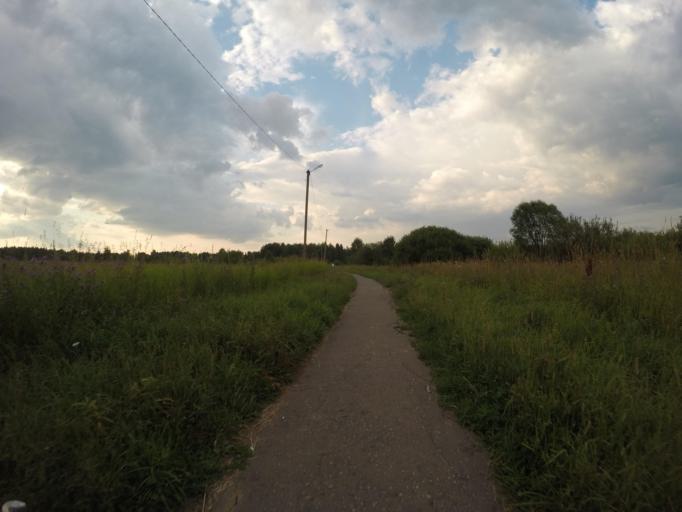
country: RU
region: Moskovskaya
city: Rechitsy
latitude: 55.6002
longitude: 38.5061
